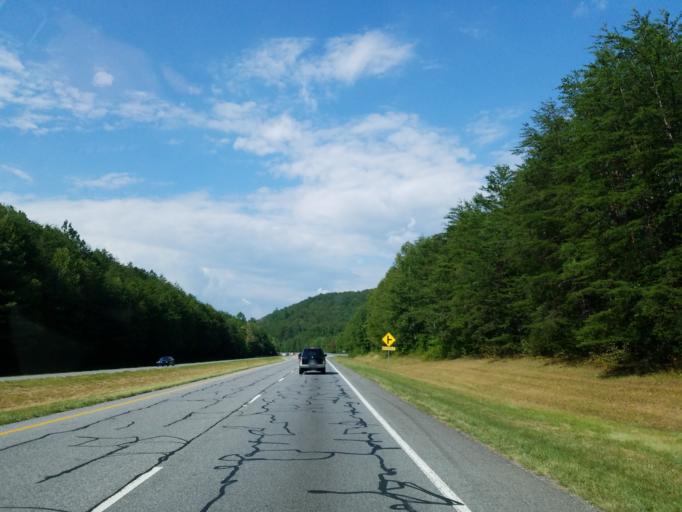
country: US
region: Georgia
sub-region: Gilmer County
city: Ellijay
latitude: 34.7573
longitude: -84.4059
